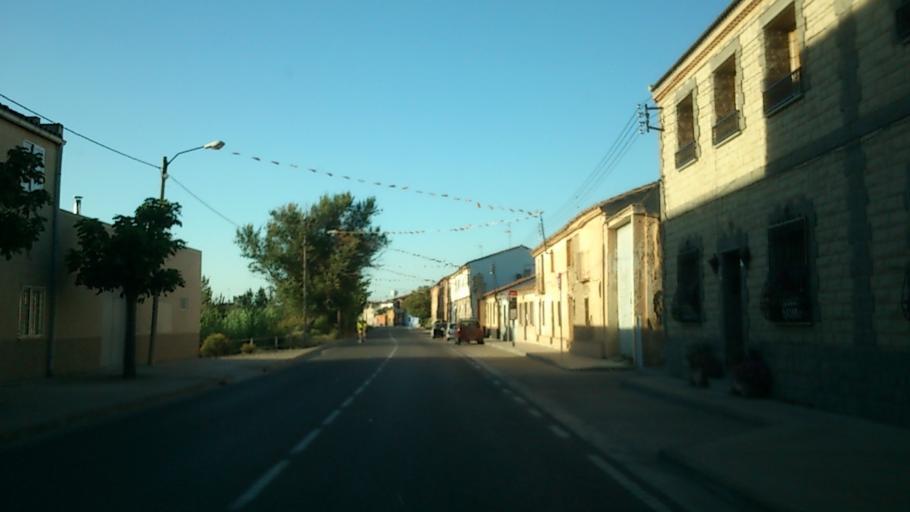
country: ES
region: Aragon
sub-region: Provincia de Zaragoza
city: Zaragoza
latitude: 41.6808
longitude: -0.8294
